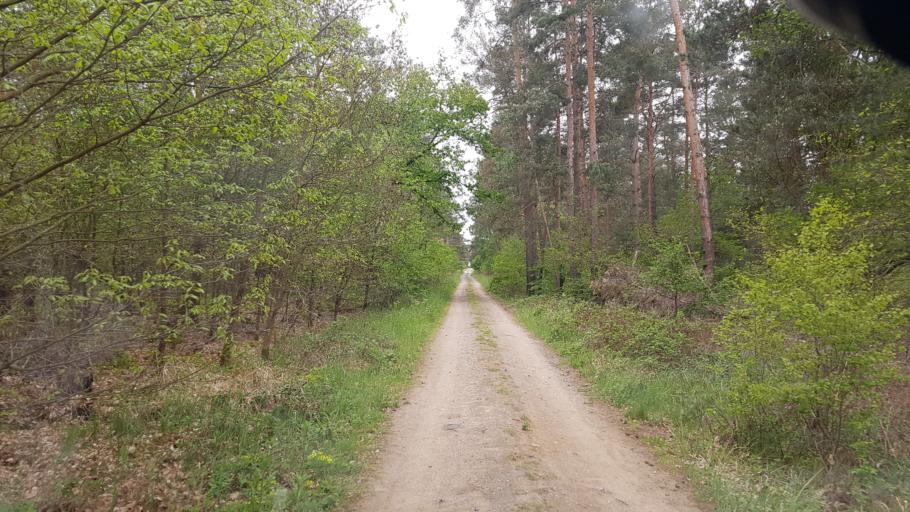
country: DE
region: Brandenburg
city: Elsterwerda
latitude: 51.5036
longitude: 13.5040
